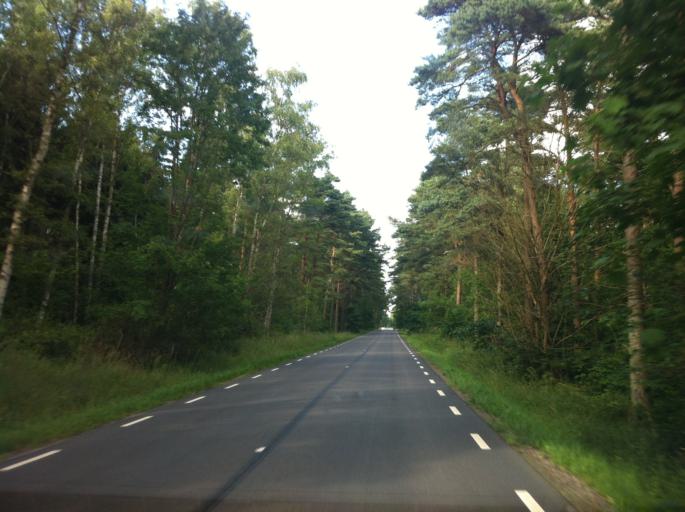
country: SE
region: Skane
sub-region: Simrishamns Kommun
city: Simrishamn
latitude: 55.4457
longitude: 14.2489
